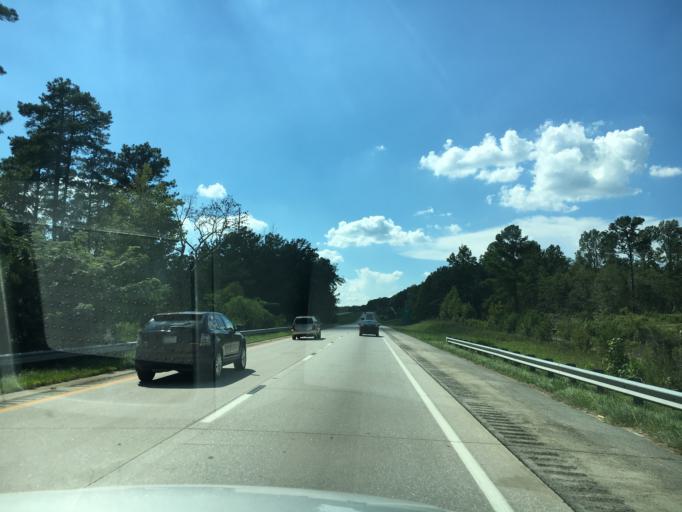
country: US
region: South Carolina
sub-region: Laurens County
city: Clinton
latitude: 34.5155
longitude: -81.8787
